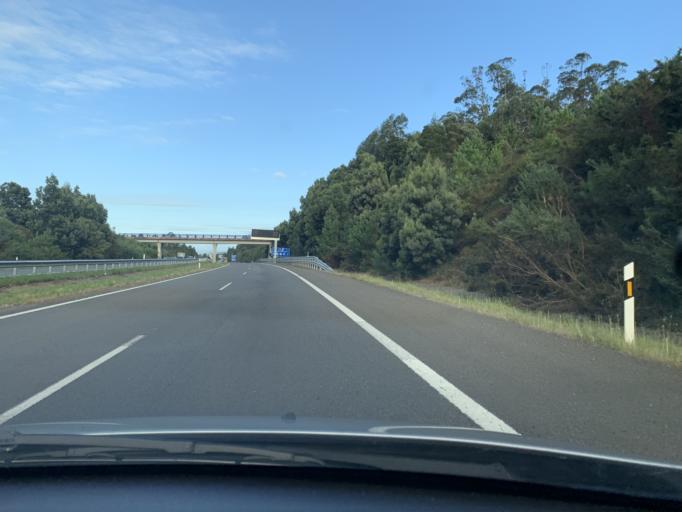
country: ES
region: Galicia
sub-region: Provincia de Lugo
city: Barreiros
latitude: 43.5385
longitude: -7.1680
